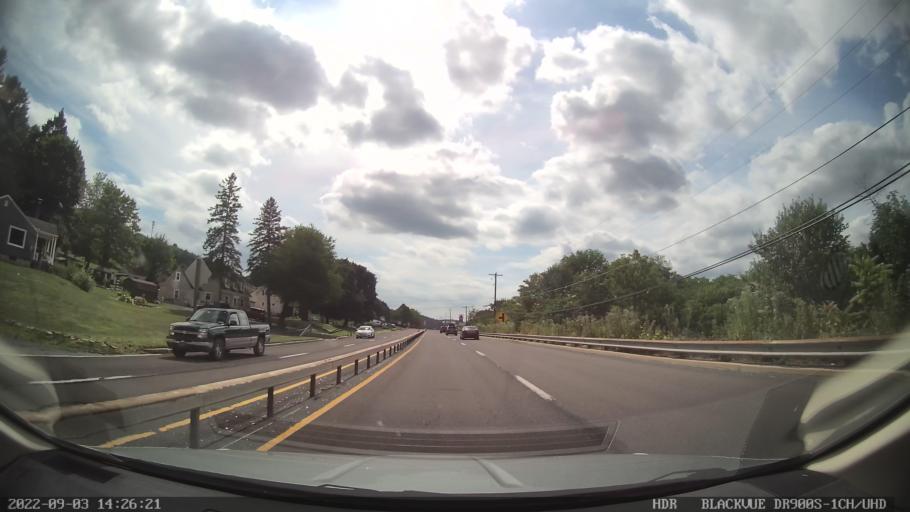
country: US
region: Pennsylvania
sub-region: Carbon County
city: Weissport East
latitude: 40.8365
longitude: -75.6873
